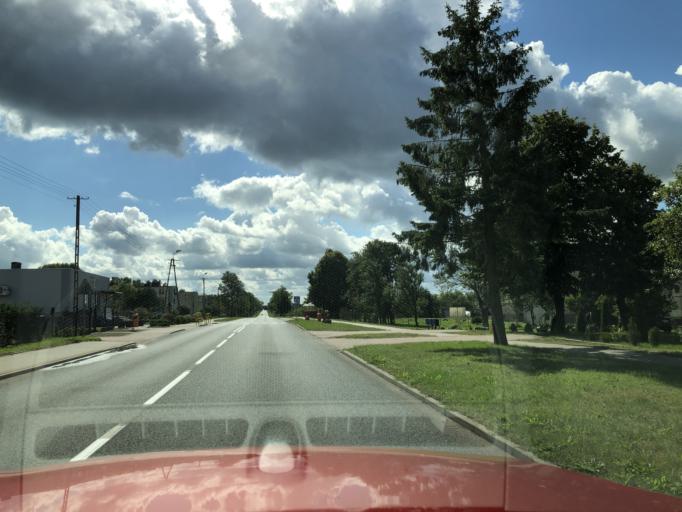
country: PL
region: West Pomeranian Voivodeship
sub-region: Powiat szczecinecki
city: Bialy Bor
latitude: 53.8286
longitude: 16.8398
